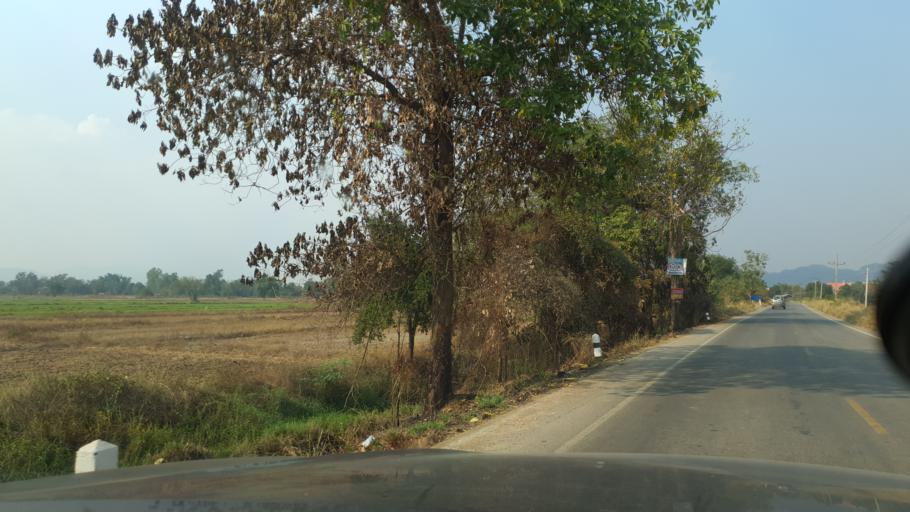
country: TH
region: Sukhothai
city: Ban Dan Lan Hoi
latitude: 17.1067
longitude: 99.5508
